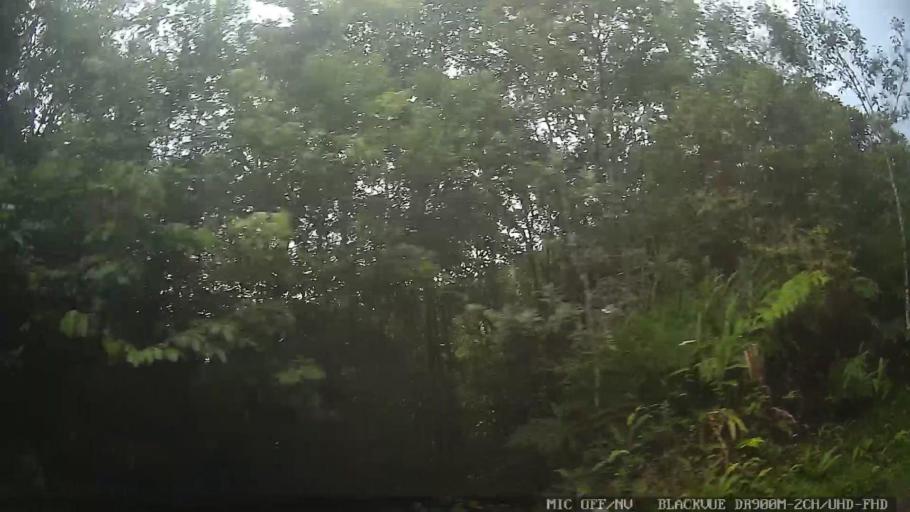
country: BR
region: Sao Paulo
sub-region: Rio Grande Da Serra
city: Rio Grande da Serra
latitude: -23.6936
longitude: -46.3291
